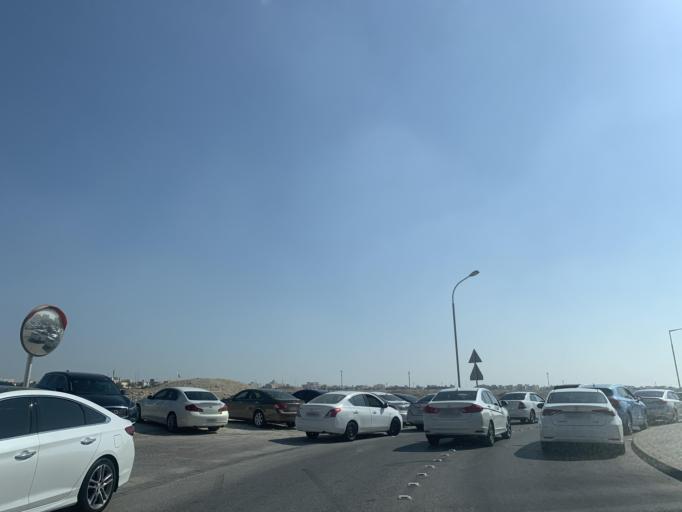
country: BH
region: Central Governorate
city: Madinat Hamad
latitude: 26.1244
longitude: 50.4964
